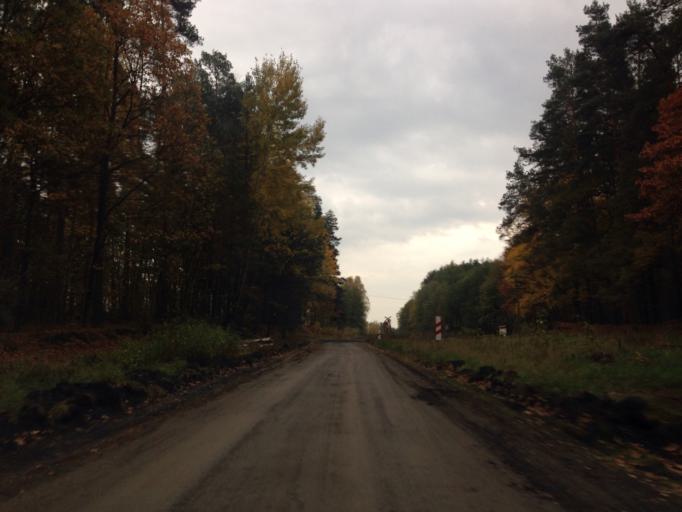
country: PL
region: Kujawsko-Pomorskie
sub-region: Powiat brodnicki
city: Bartniczka
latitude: 53.2668
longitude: 19.5800
